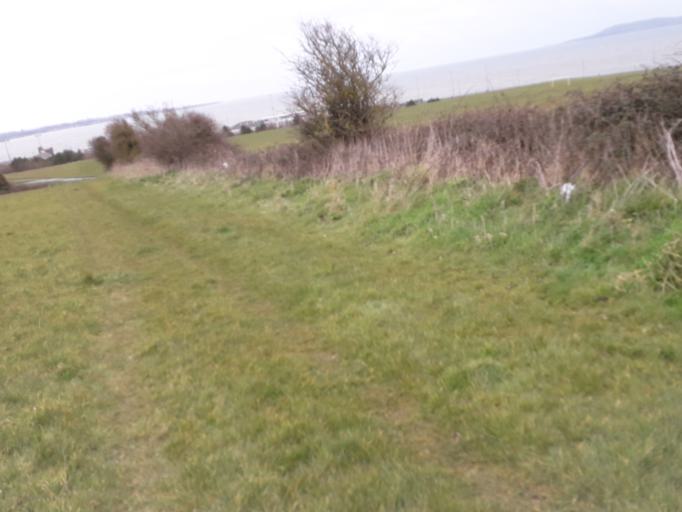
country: IE
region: Leinster
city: Portmarnock
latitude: 53.4402
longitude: -6.1291
